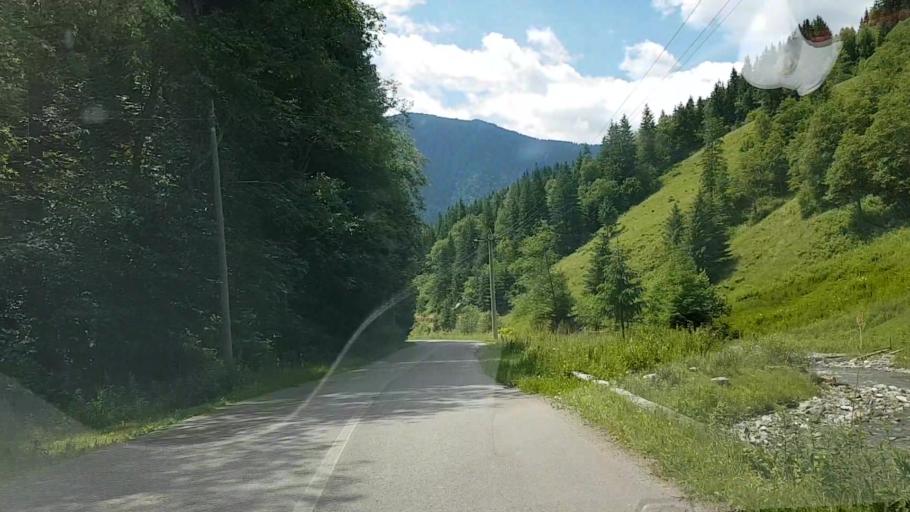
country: RO
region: Suceava
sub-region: Comuna Crucea
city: Crucea
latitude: 47.4101
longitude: 25.5800
